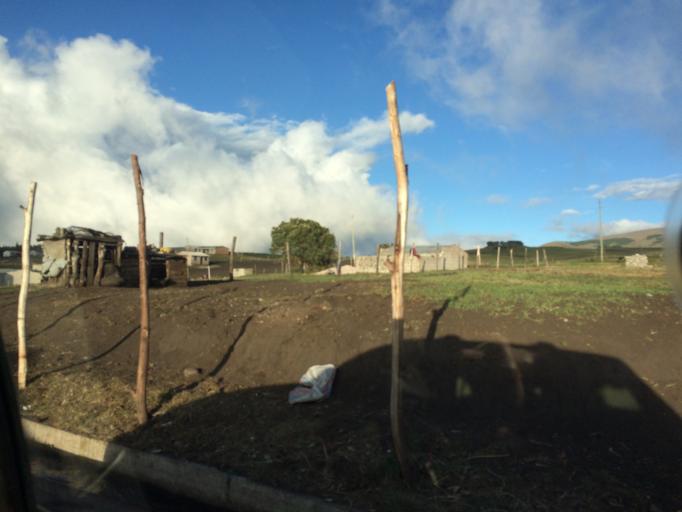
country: EC
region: Chimborazo
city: Alausi
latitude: -2.1331
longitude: -78.7190
